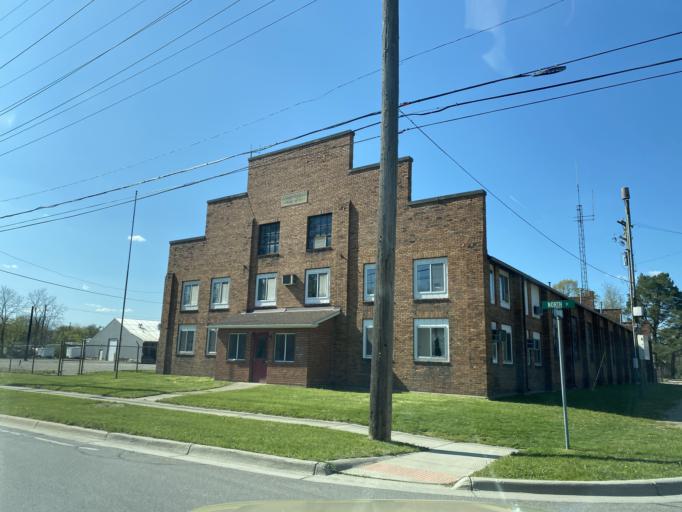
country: US
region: Michigan
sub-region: Livingston County
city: Howell
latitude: 42.6057
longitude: -83.9181
